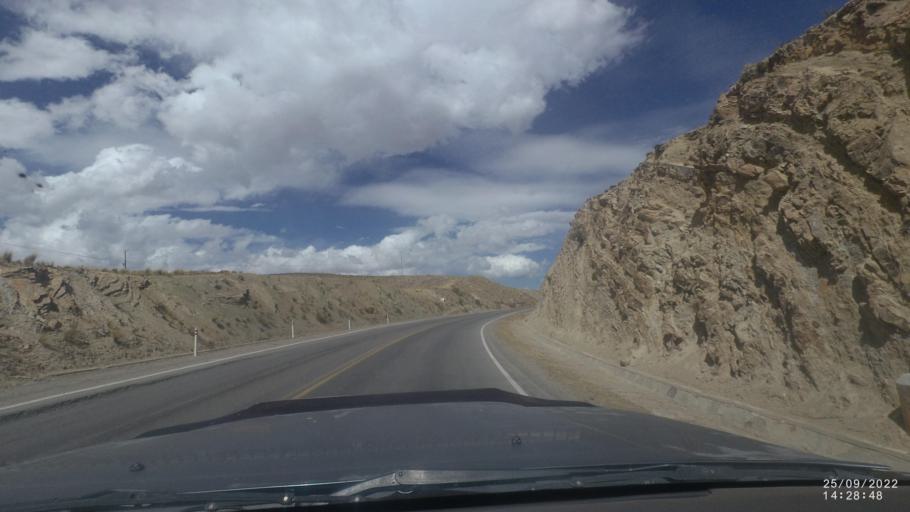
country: BO
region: Cochabamba
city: Sipe Sipe
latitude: -17.7106
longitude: -66.6648
